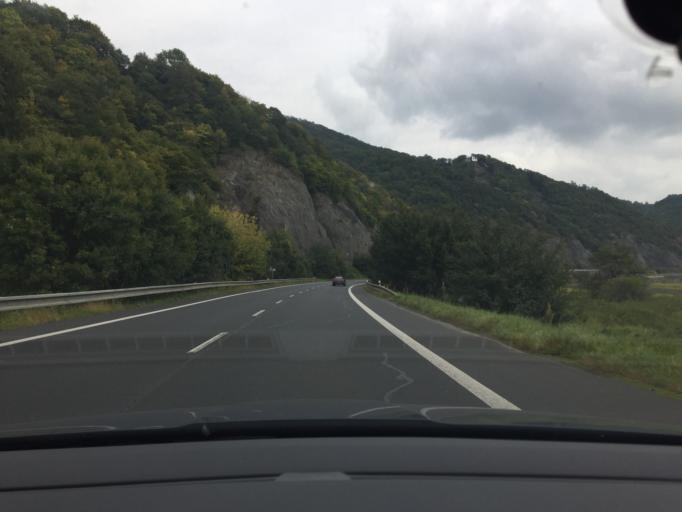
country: CZ
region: Ustecky
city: Povrly
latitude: 50.6780
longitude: 14.1661
